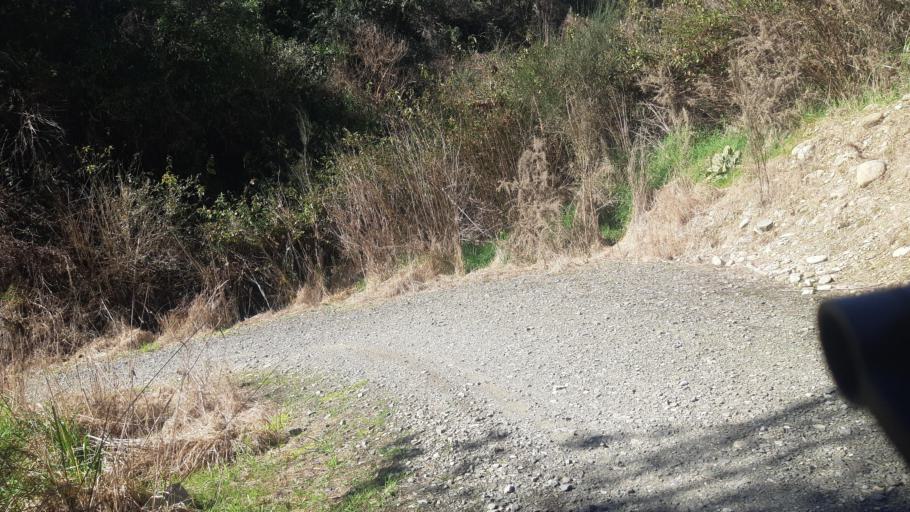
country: NZ
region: Tasman
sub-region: Tasman District
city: Wakefield
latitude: -41.4402
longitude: 172.9843
